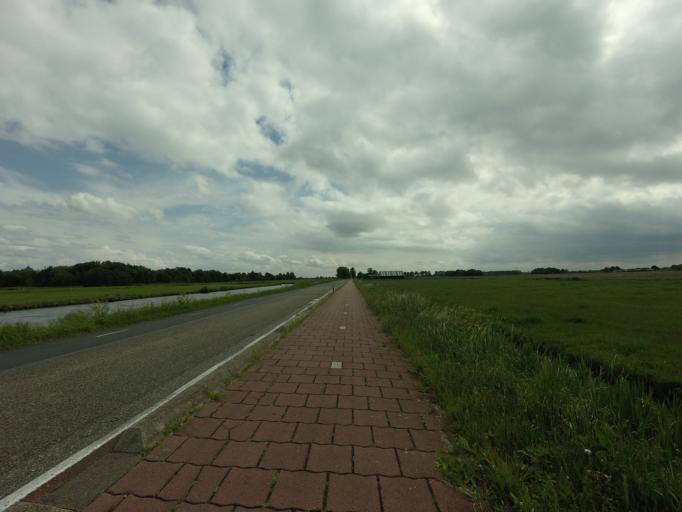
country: NL
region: Utrecht
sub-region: Gemeente De Ronde Venen
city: Mijdrecht
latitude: 52.2405
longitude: 4.9037
